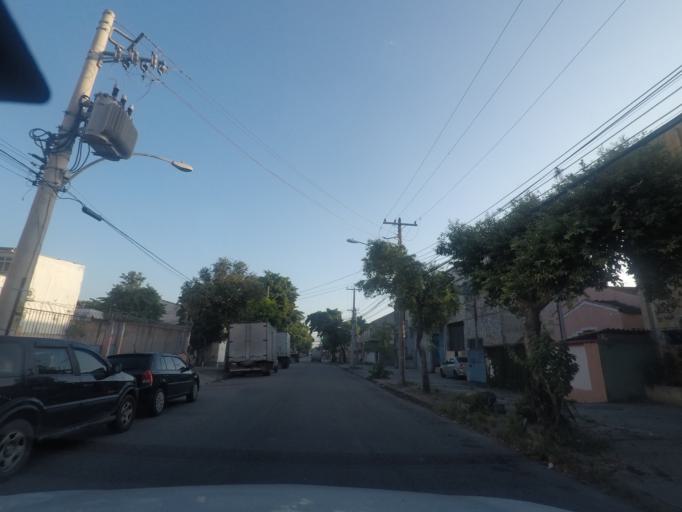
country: BR
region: Rio de Janeiro
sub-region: Duque De Caxias
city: Duque de Caxias
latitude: -22.8330
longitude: -43.2752
